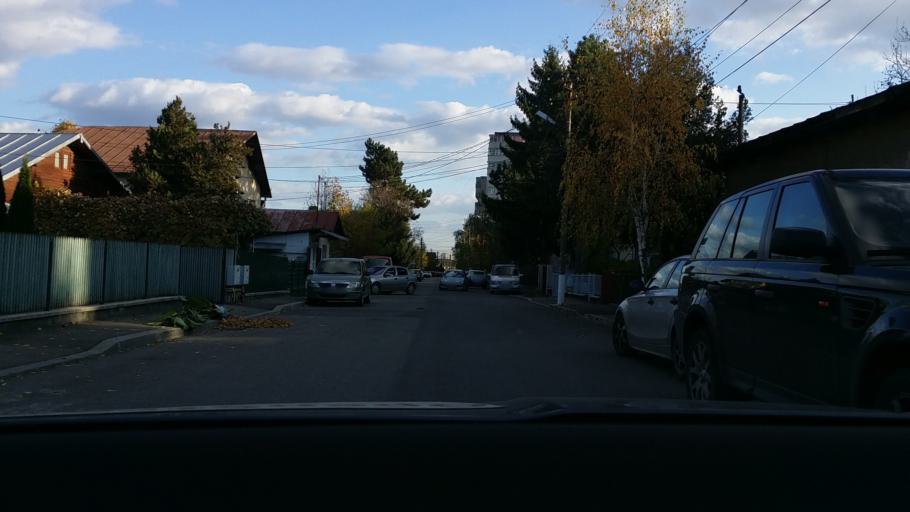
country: RO
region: Prahova
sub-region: Municipiul Campina
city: Campina
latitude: 45.1292
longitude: 25.7408
